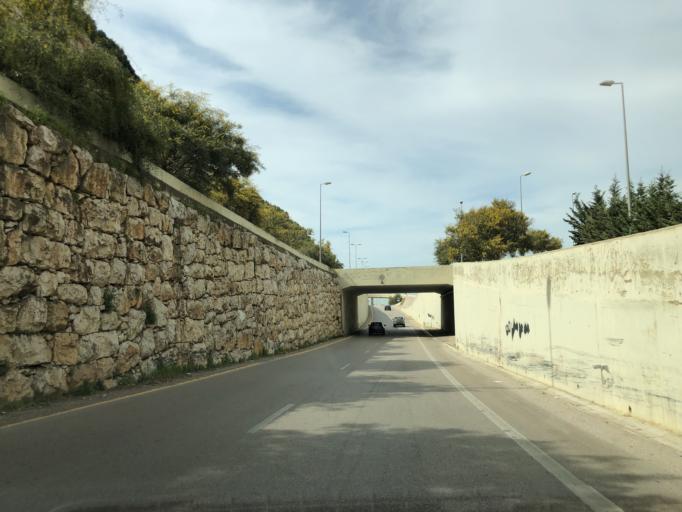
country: LB
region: Mont-Liban
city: Jdaidet el Matn
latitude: 33.8957
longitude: 35.6506
